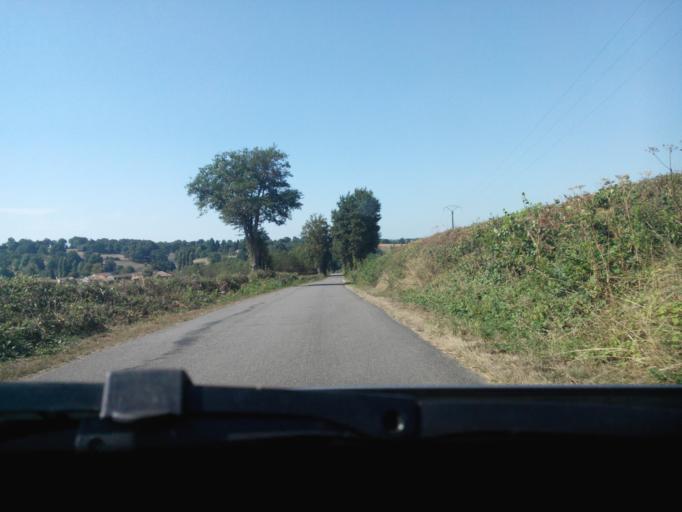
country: FR
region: Poitou-Charentes
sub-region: Departement de la Charente
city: Brigueuil
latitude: 45.9687
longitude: 0.7936
